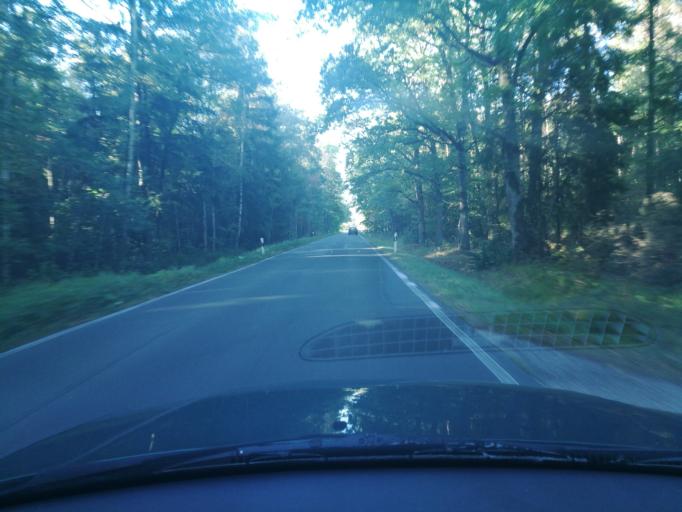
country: DE
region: Bavaria
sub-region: Regierungsbezirk Mittelfranken
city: Hessdorf
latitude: 49.6214
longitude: 10.9387
